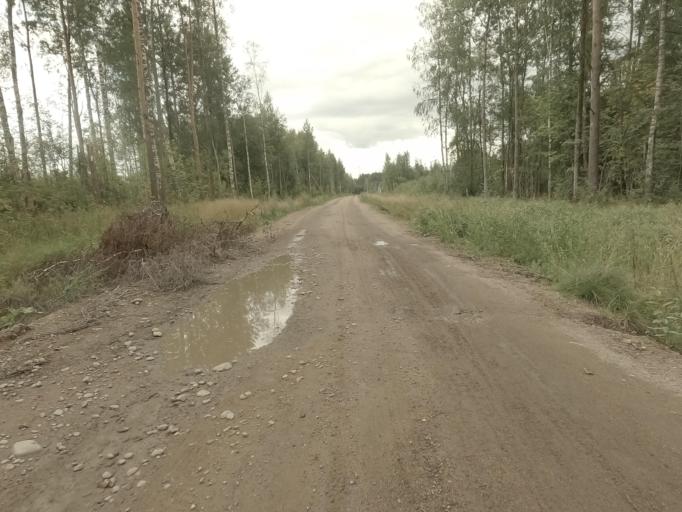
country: RU
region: Leningrad
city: Kirovsk
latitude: 59.9022
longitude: 31.0033
